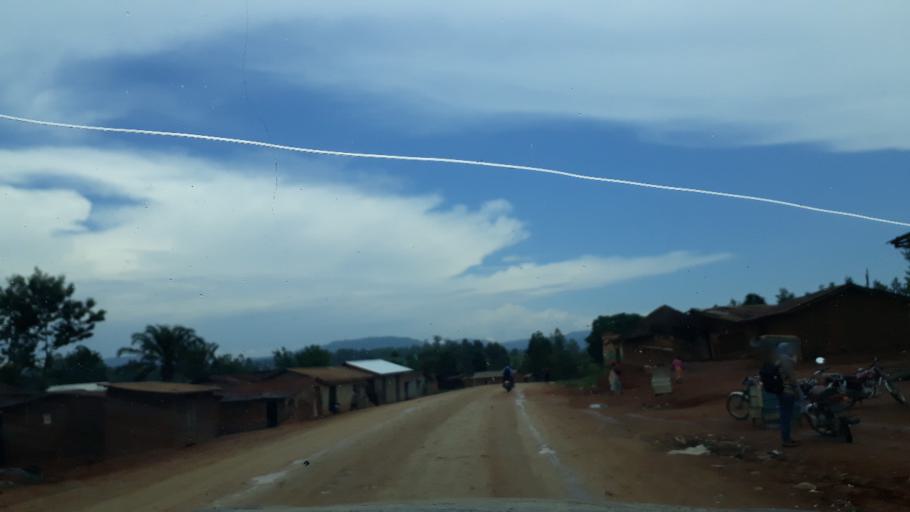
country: CD
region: Eastern Province
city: Bunia
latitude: 1.6443
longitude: 30.2690
